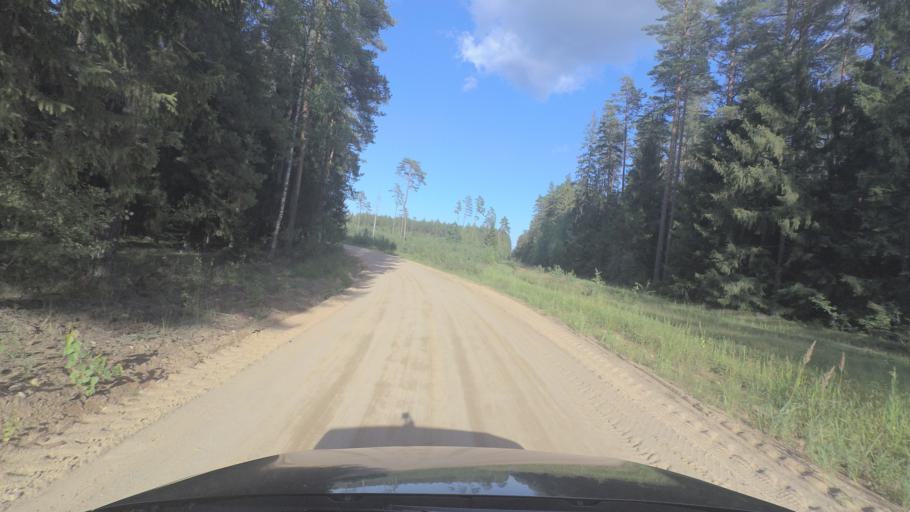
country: LT
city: Pabrade
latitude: 55.1536
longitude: 25.7841
